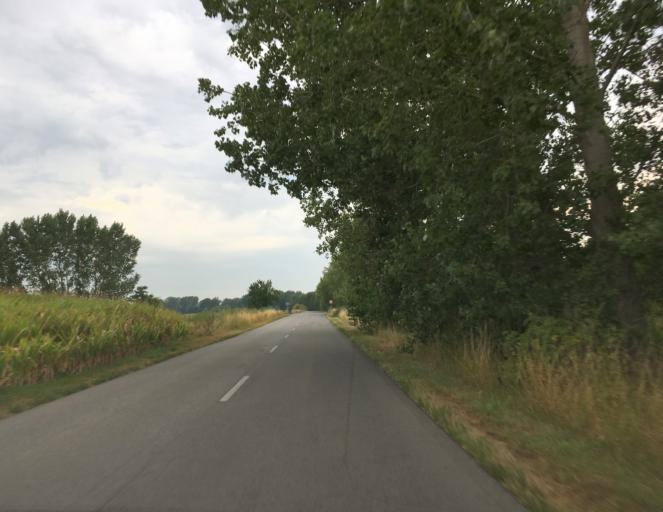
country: SK
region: Trnavsky
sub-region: Okres Dunajska Streda
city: Velky Meder
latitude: 47.9120
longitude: 17.6881
